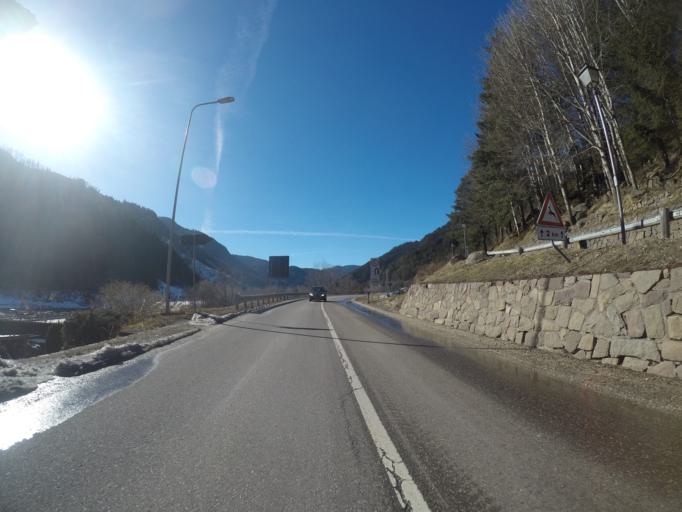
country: IT
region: Trentino-Alto Adige
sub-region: Provincia di Trento
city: Castello Molina di Fiemme
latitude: 46.2665
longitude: 11.4057
